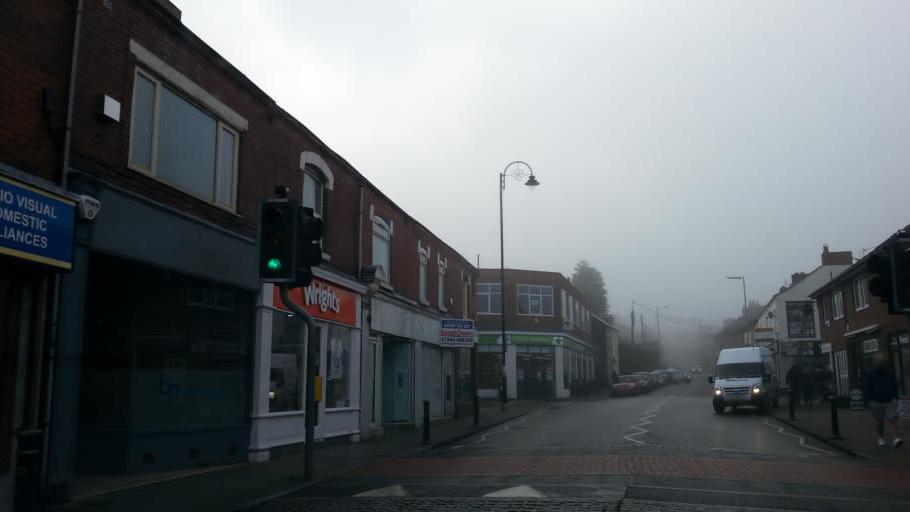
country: GB
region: England
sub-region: Staffordshire
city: Biddulph
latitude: 53.1155
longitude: -2.1762
